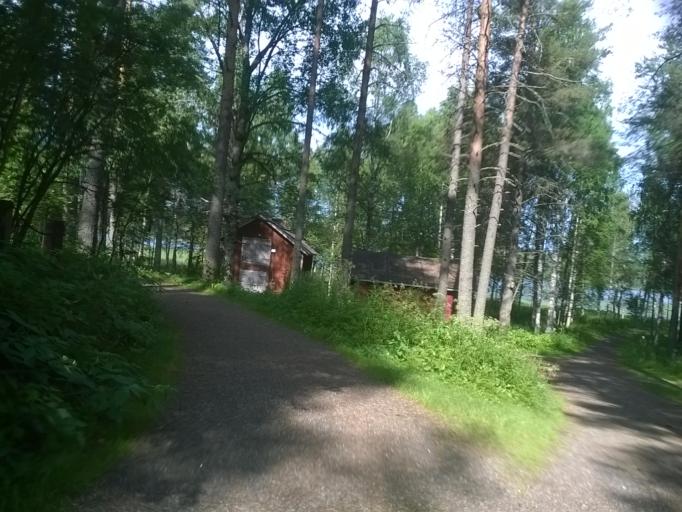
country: FI
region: Kainuu
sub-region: Kehys-Kainuu
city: Kuhmo
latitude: 64.1324
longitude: 29.5245
